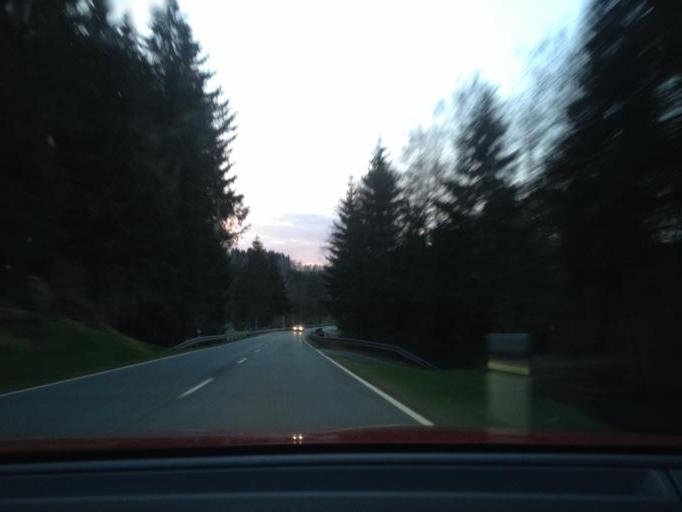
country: DE
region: Bavaria
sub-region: Upper Palatinate
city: Neusorg
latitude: 49.9151
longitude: 11.9688
